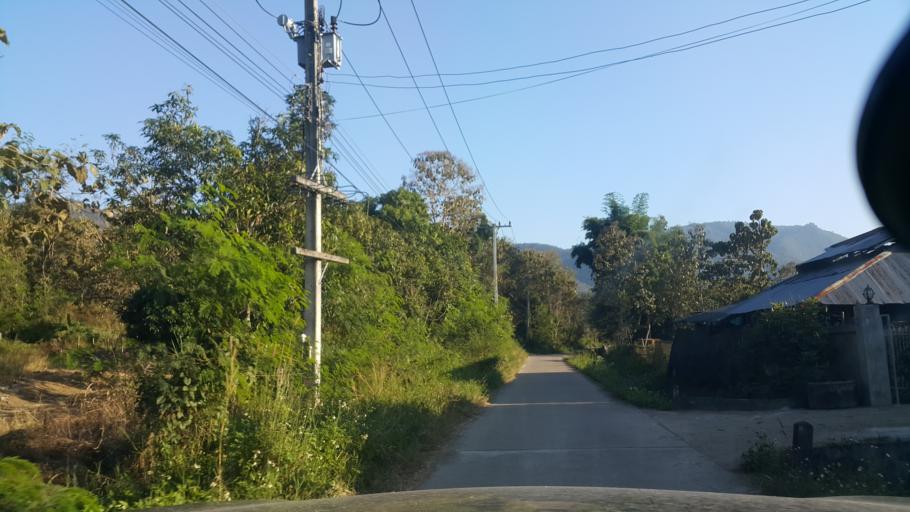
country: TH
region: Chiang Mai
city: Mae On
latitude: 18.7697
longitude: 99.2652
